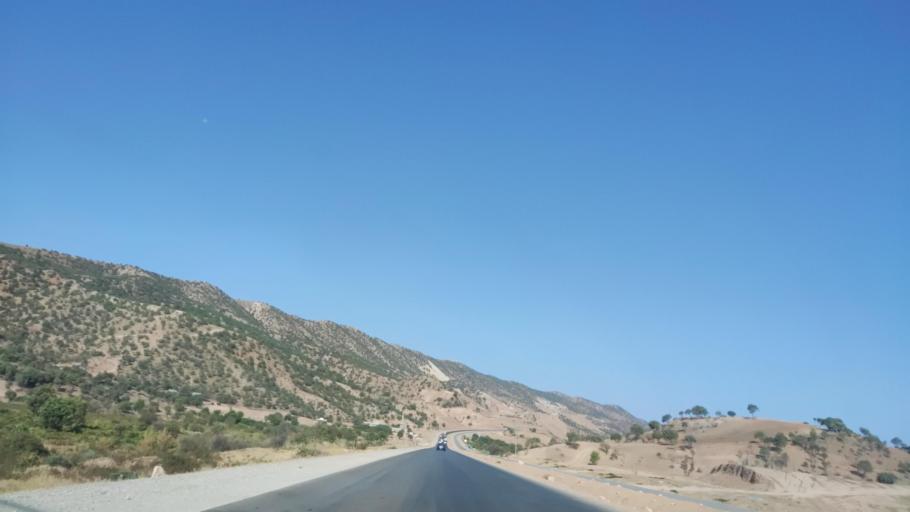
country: IQ
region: Arbil
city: Shaqlawah
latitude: 36.4304
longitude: 44.3237
